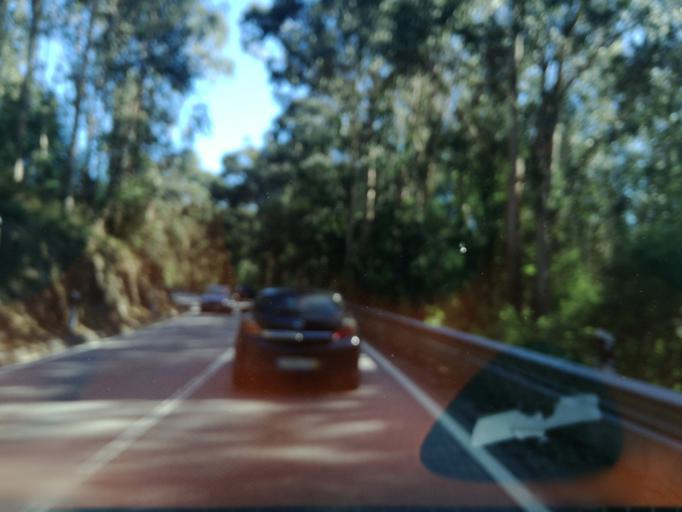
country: PT
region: Porto
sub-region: Pacos de Ferreira
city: Seroa
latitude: 41.2570
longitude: -8.4511
